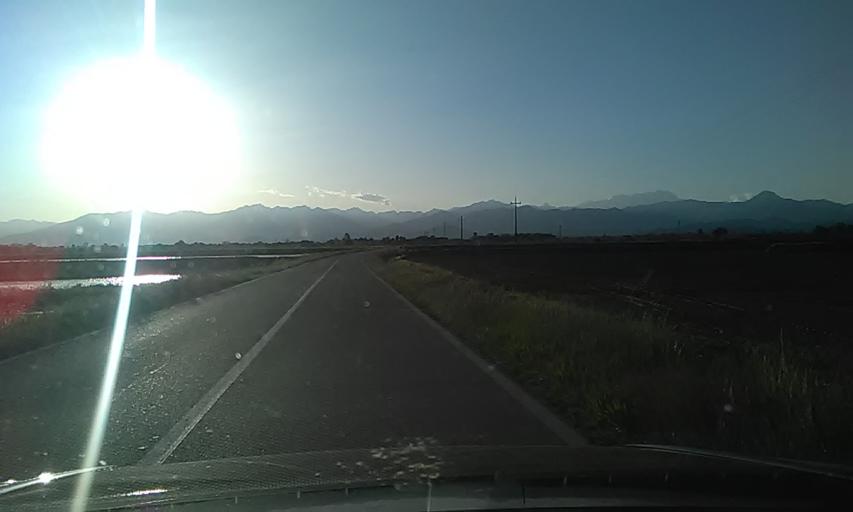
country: IT
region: Piedmont
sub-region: Provincia di Vercelli
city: Rovasenda
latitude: 45.5230
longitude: 8.3361
